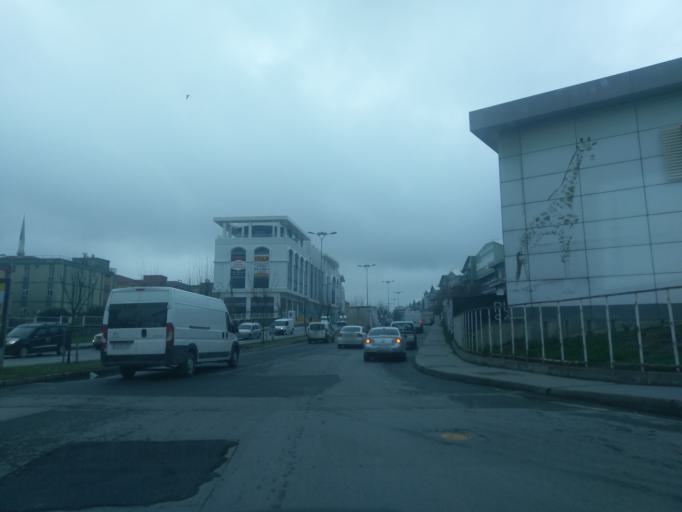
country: TR
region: Istanbul
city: Basaksehir
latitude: 41.0801
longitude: 28.7937
